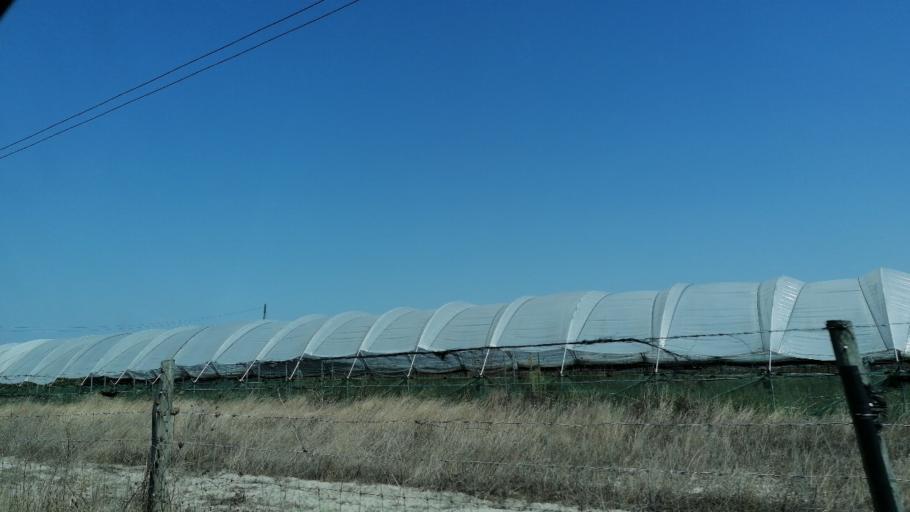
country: PT
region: Santarem
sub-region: Benavente
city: Poceirao
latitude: 38.7195
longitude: -8.7106
